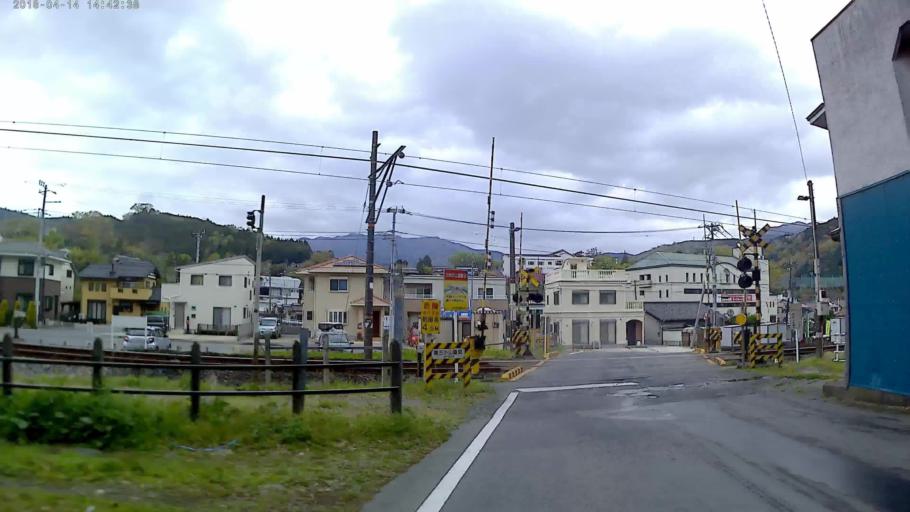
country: JP
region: Shizuoka
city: Gotemba
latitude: 35.3584
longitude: 138.9871
